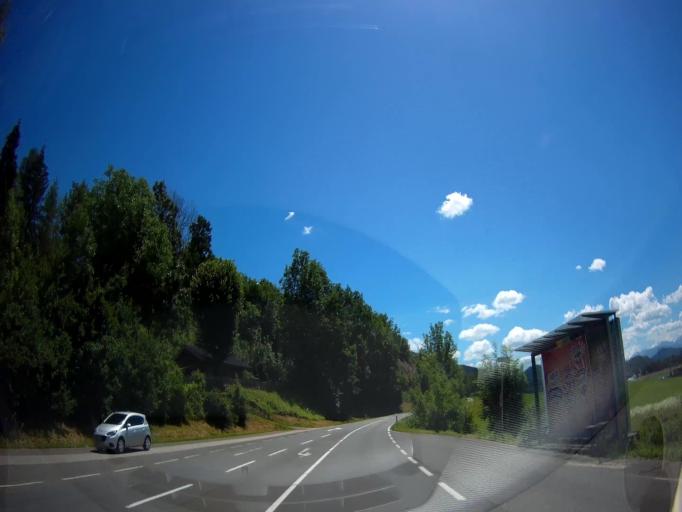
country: AT
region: Carinthia
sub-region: Politischer Bezirk Sankt Veit an der Glan
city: Sankt Veit an der Glan
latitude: 46.7447
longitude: 14.3896
